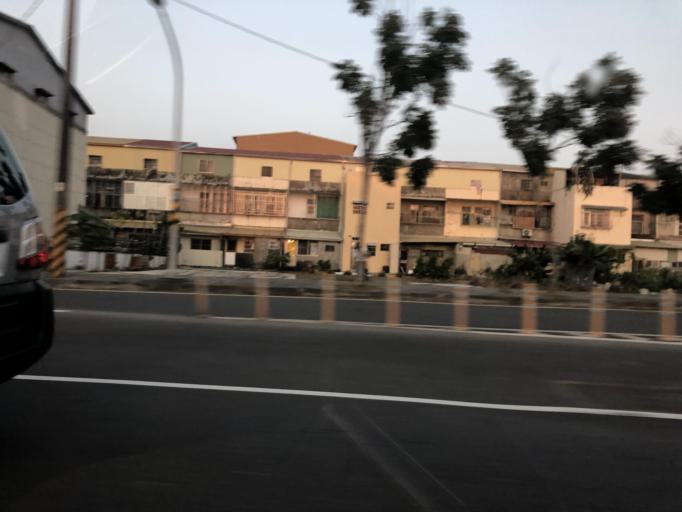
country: TW
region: Taiwan
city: Xinying
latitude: 23.3017
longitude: 120.2934
